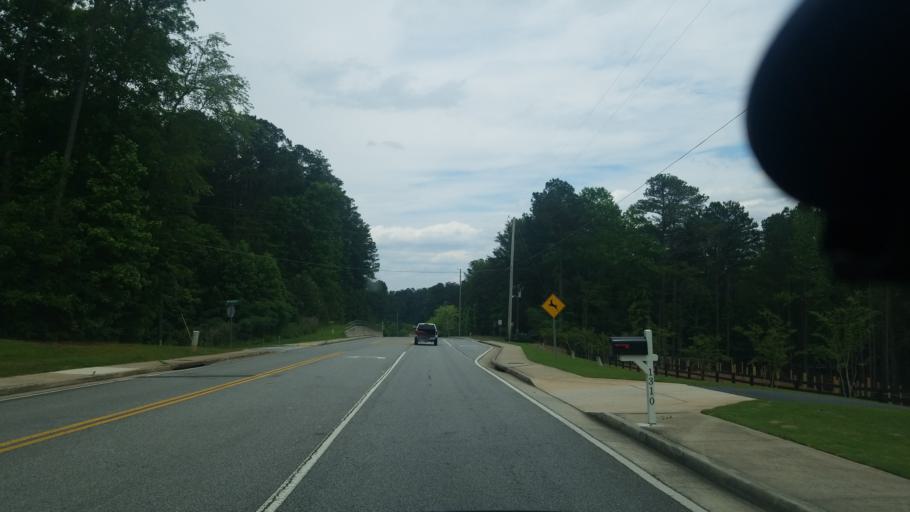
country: US
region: Georgia
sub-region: Forsyth County
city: Cumming
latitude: 34.1952
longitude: -84.1118
